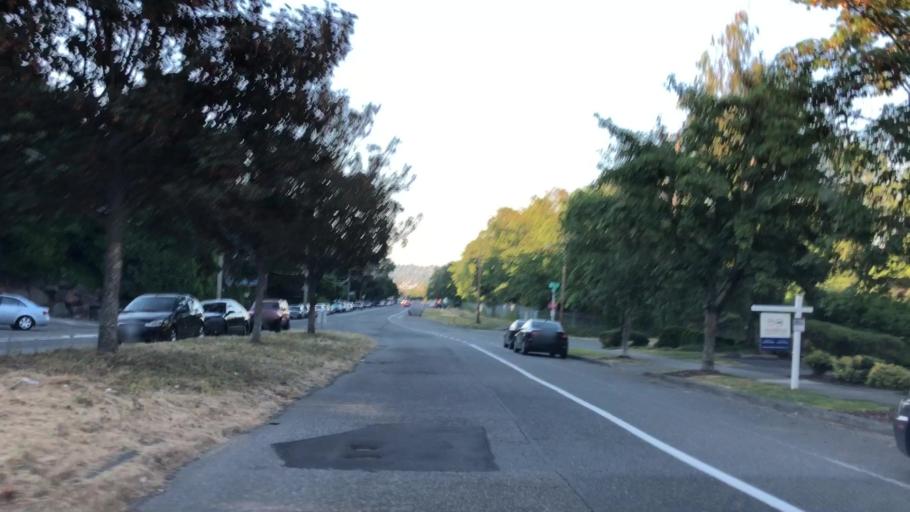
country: US
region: Washington
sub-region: King County
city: Seattle
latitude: 47.6400
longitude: -122.3867
